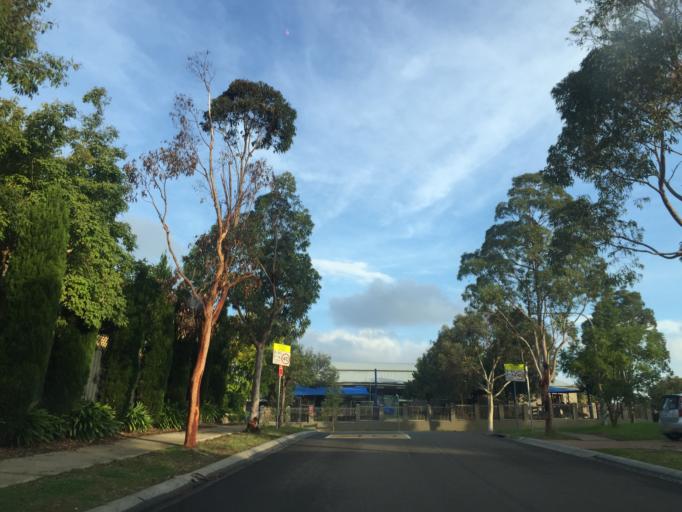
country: AU
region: New South Wales
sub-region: The Hills Shire
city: Glenhaven
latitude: -33.7065
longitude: 150.9768
